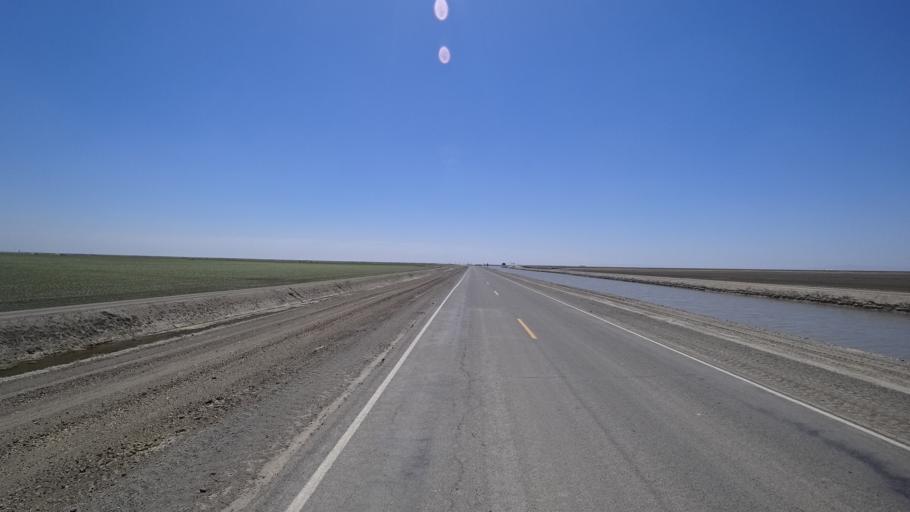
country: US
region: California
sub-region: Kings County
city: Corcoran
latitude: 36.0552
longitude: -119.6437
